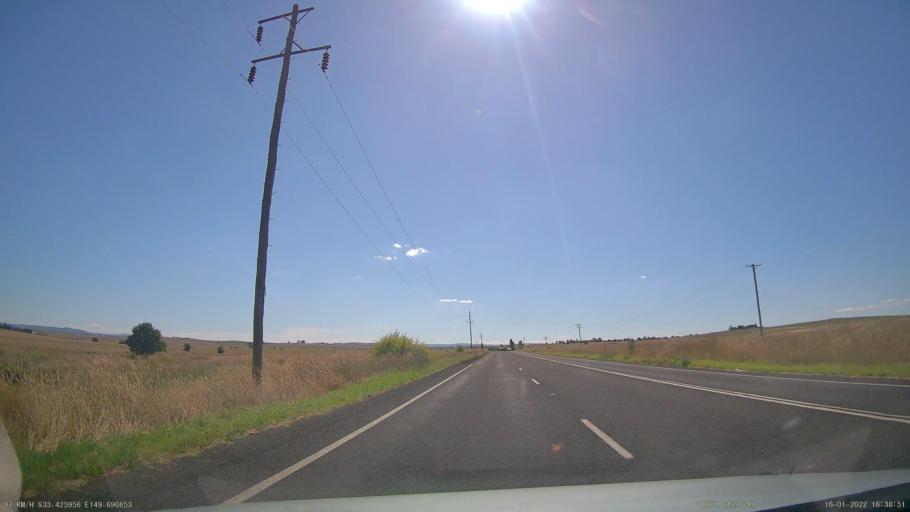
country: AU
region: New South Wales
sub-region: Bathurst Regional
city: Kelso
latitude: -33.4261
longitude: 149.6902
